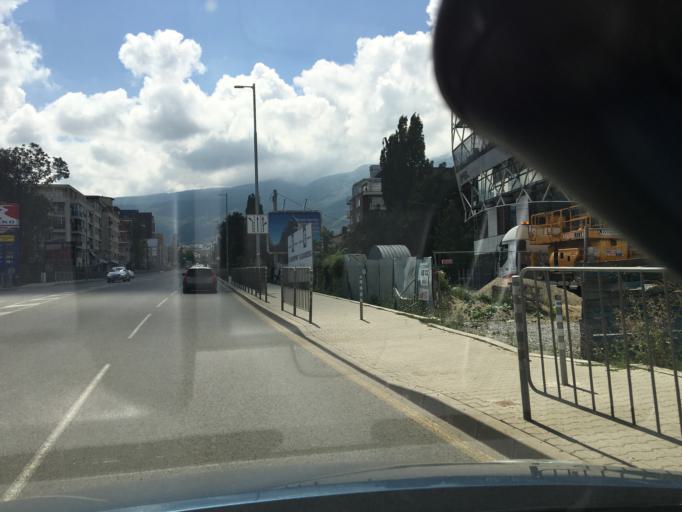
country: BG
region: Sofia-Capital
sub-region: Stolichna Obshtina
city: Sofia
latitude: 42.6517
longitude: 23.3159
